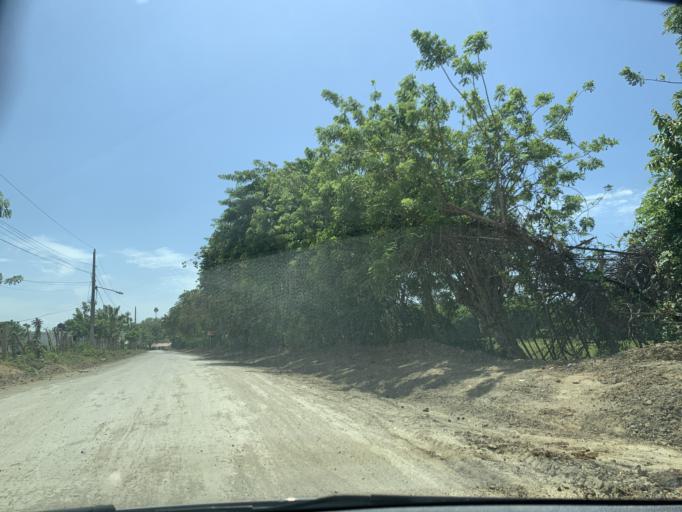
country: DO
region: Puerto Plata
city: Luperon
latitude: 19.8827
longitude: -70.8349
